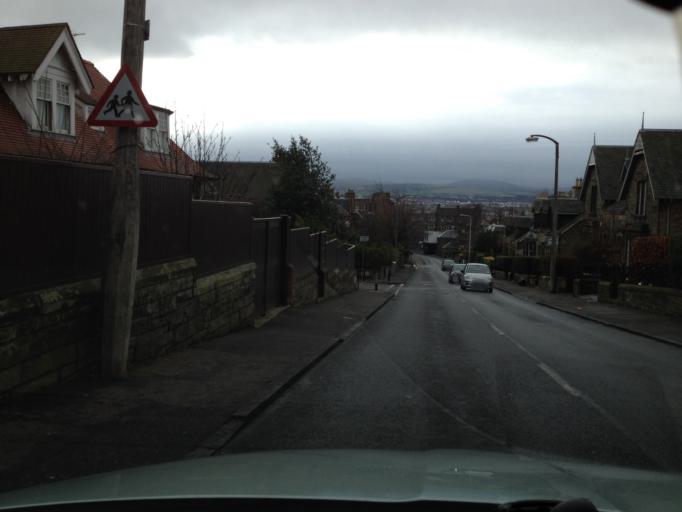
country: GB
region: Scotland
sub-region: Edinburgh
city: Colinton
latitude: 55.9448
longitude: -3.2806
